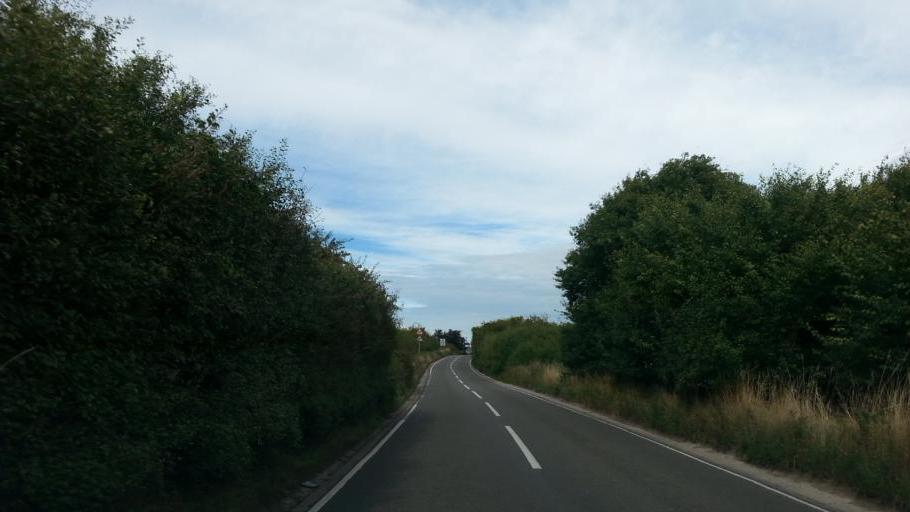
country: GB
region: England
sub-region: Cambridgeshire
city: Cambridge
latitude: 52.1748
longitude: 0.1645
